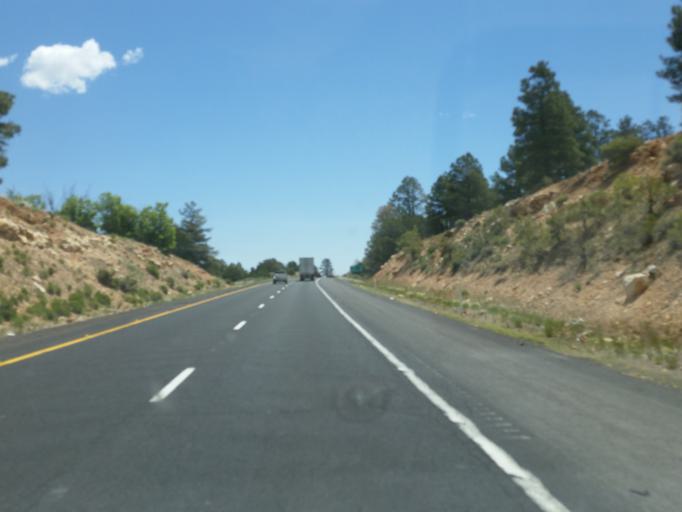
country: US
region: Arizona
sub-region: Coconino County
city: Flagstaff
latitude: 35.2182
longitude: -111.5657
